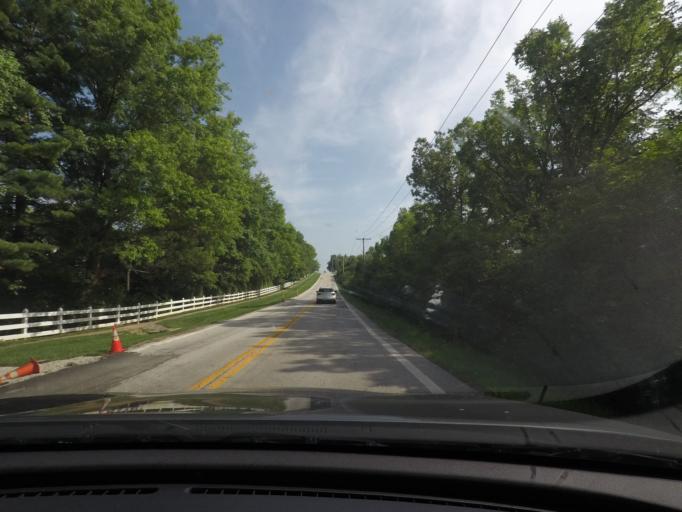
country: US
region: Missouri
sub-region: Saint Louis County
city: Town and Country
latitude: 38.6332
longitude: -90.4809
